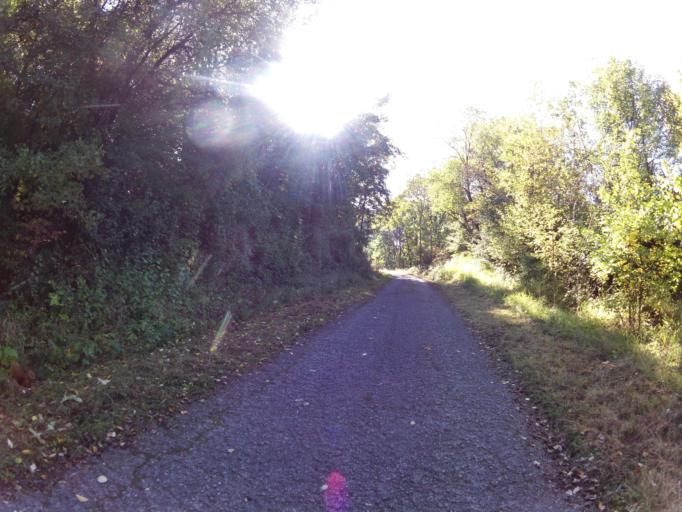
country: DE
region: Bavaria
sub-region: Regierungsbezirk Unterfranken
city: Ochsenfurt
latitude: 49.6811
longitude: 10.0510
